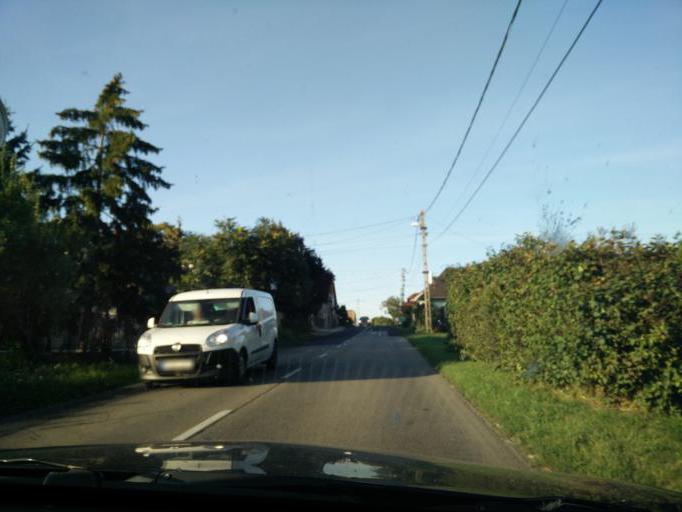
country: HU
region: Pest
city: Perbal
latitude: 47.5867
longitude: 18.7522
